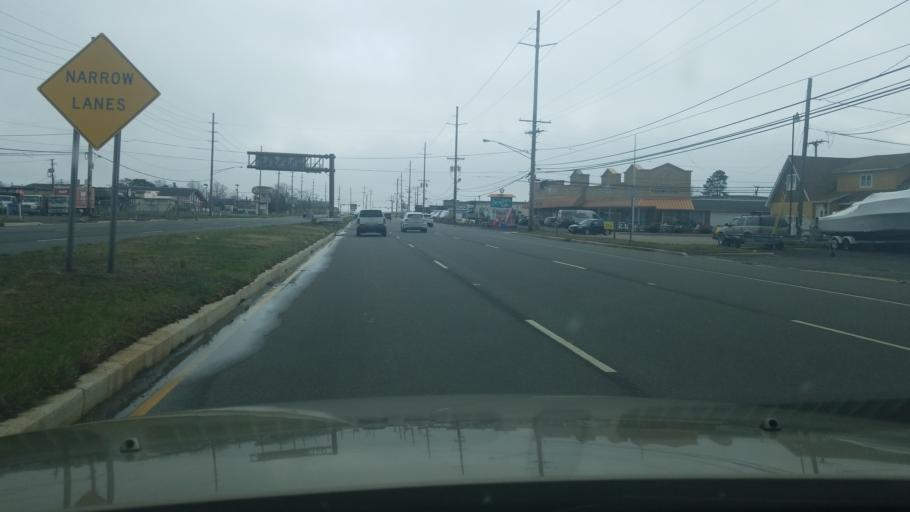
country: US
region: New Jersey
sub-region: Ocean County
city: Ocean Gate
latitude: 39.9497
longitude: -74.1205
